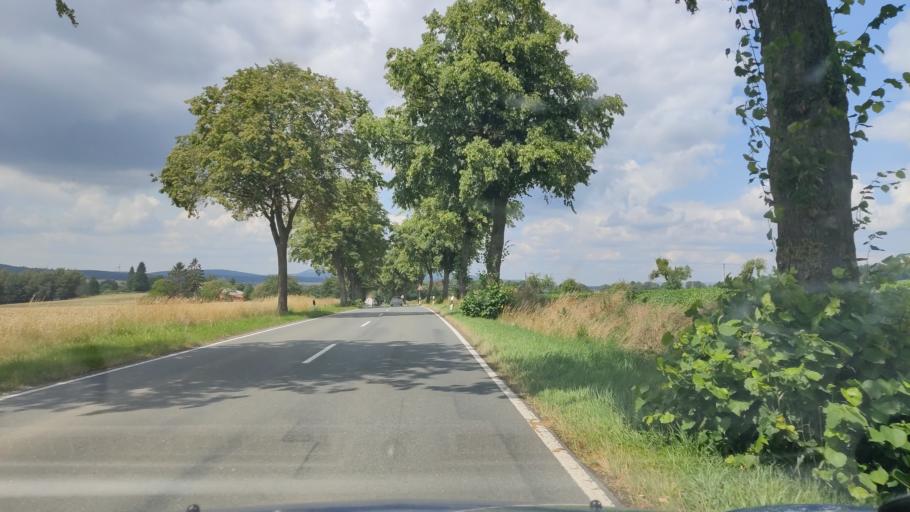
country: DE
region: Lower Saxony
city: Coppenbrugge
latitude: 52.0787
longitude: 9.5085
